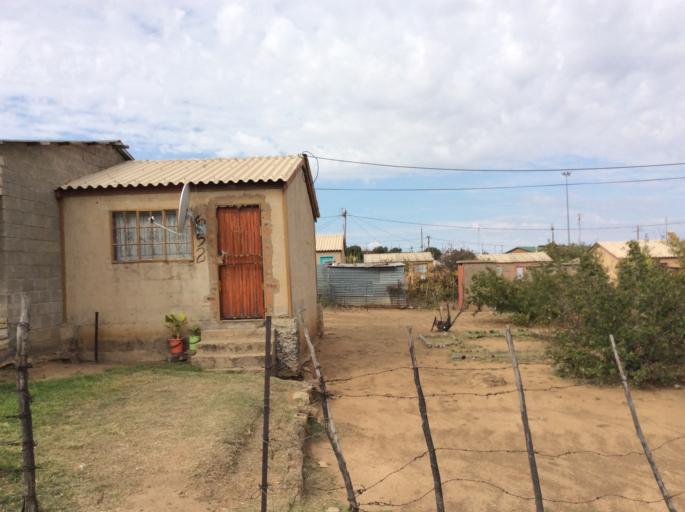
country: LS
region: Mafeteng
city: Mafeteng
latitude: -29.7179
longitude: 27.0269
